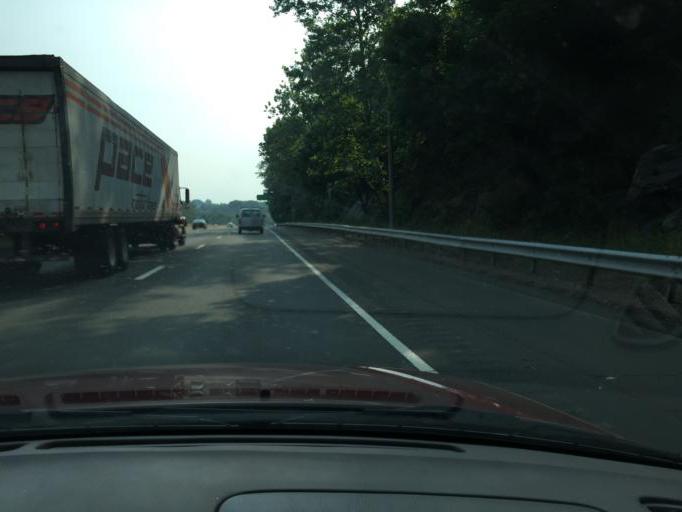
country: US
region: Connecticut
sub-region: Fairfield County
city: Greenwich
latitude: 41.0212
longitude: -73.6217
